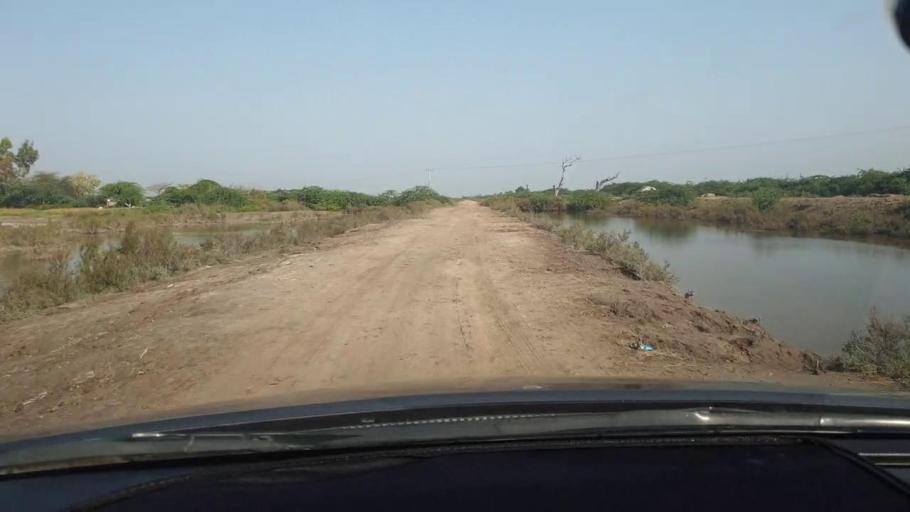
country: PK
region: Sindh
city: Tando Bago
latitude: 24.6758
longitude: 69.1694
